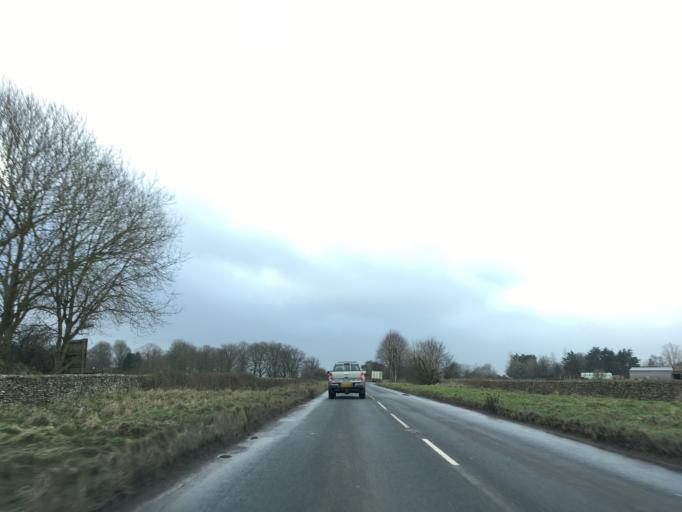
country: GB
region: England
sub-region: Gloucestershire
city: Chalford
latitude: 51.7136
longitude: -2.1368
